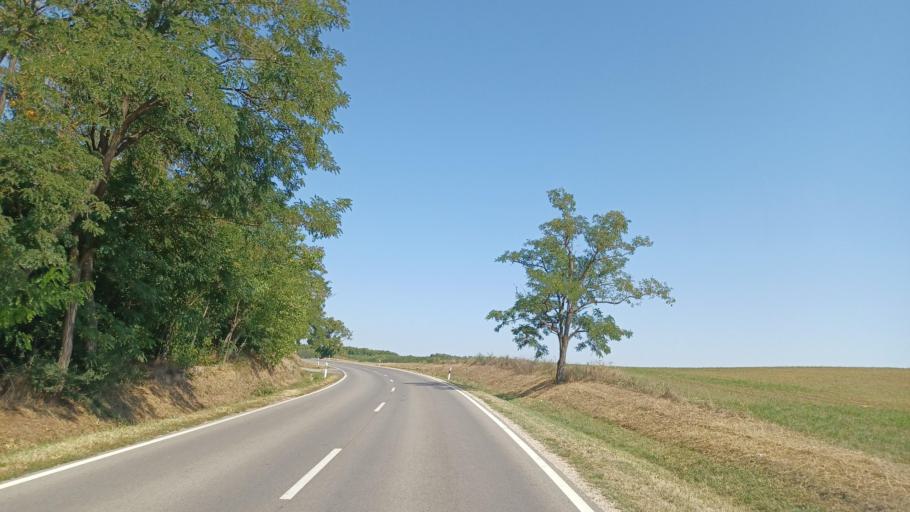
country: HU
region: Tolna
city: Nagydorog
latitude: 46.6859
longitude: 18.6715
